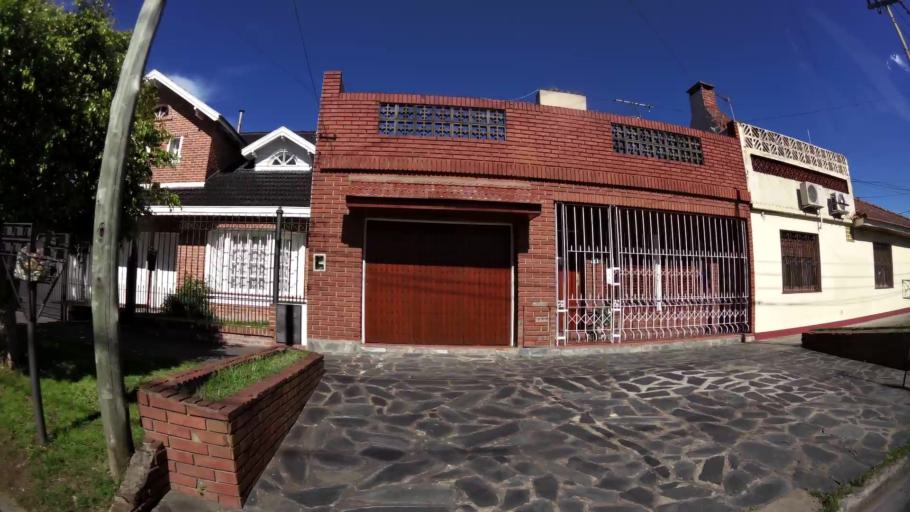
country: AR
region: Buenos Aires
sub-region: Partido de Lomas de Zamora
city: Lomas de Zamora
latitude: -34.7554
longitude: -58.4180
